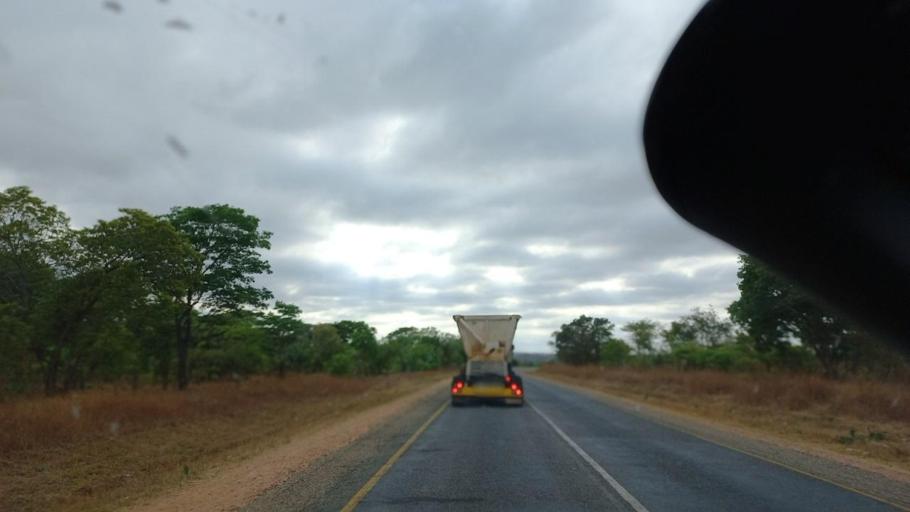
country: ZM
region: Lusaka
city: Chongwe
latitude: -15.2820
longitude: 28.7890
